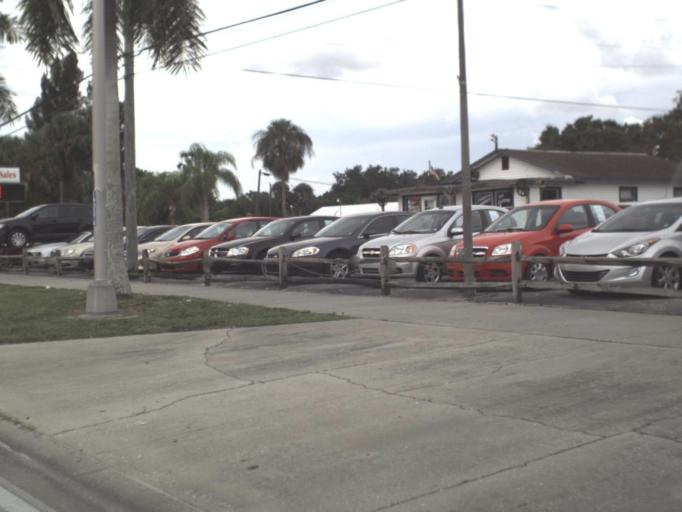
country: US
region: Florida
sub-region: Lee County
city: Tice
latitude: 26.6782
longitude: -81.8094
